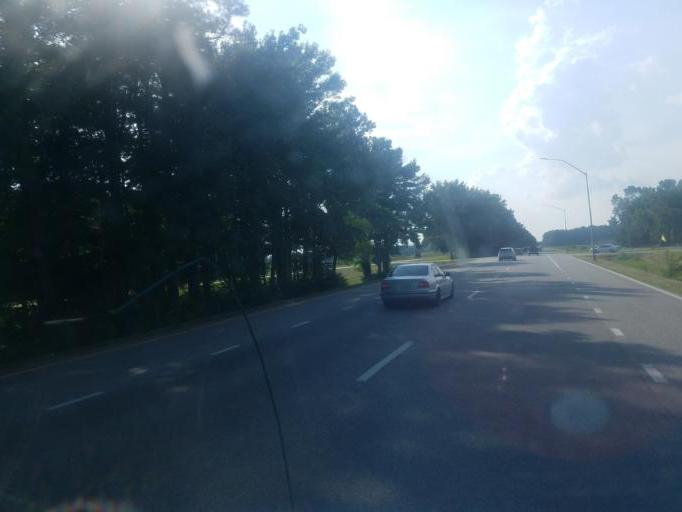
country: US
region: Maryland
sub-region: Worcester County
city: Berlin
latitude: 38.3634
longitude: -75.2597
